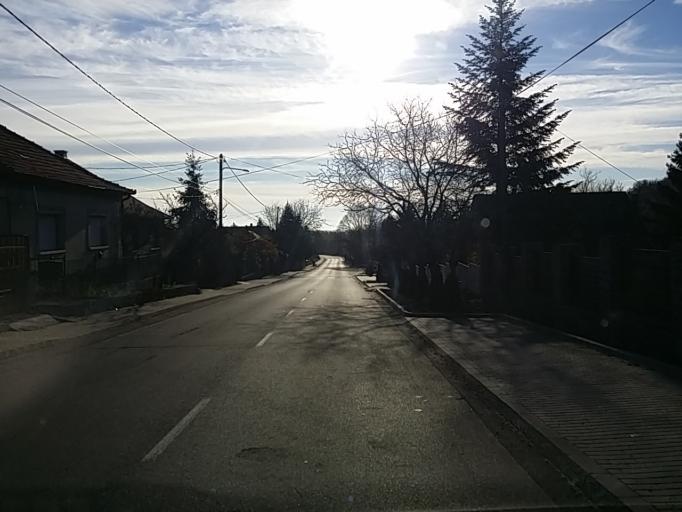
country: HU
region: Heves
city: Abasar
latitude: 47.8129
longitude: 20.0019
